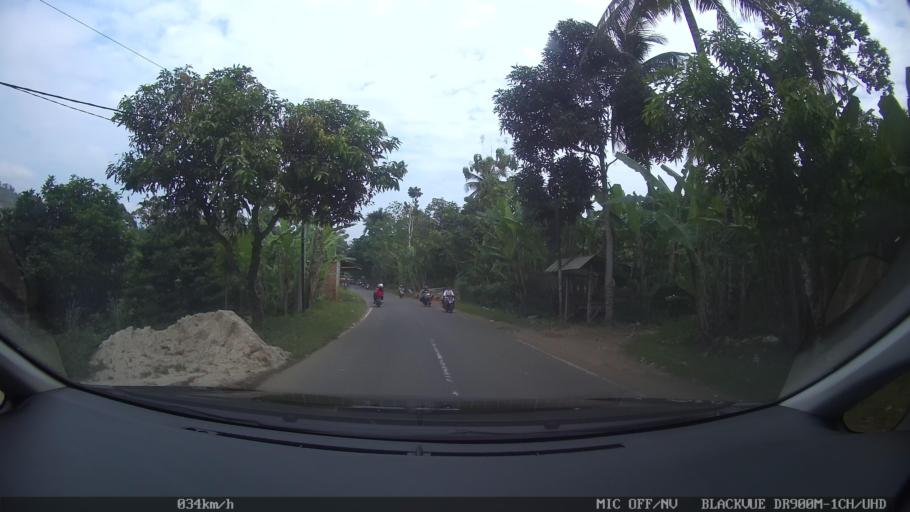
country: ID
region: Lampung
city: Bandarlampung
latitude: -5.4405
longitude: 105.2392
